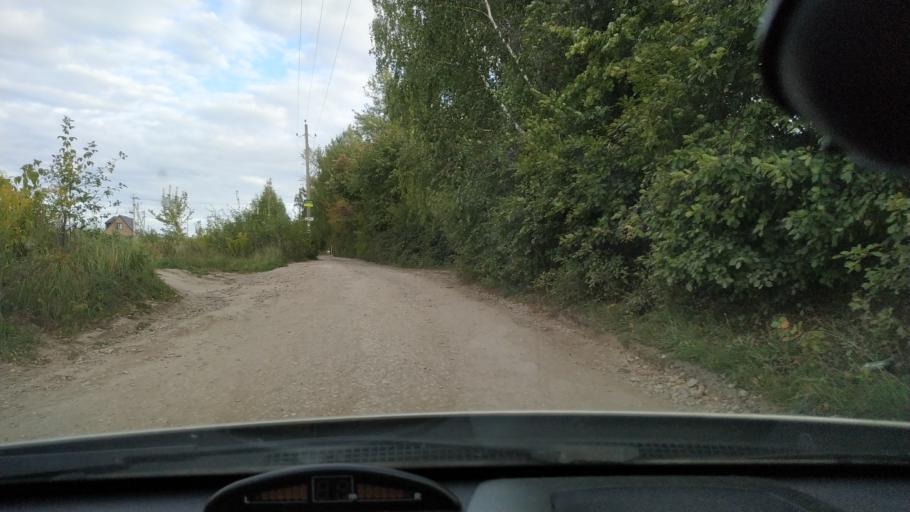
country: RU
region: Rjazan
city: Polyany
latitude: 54.5605
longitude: 39.8767
